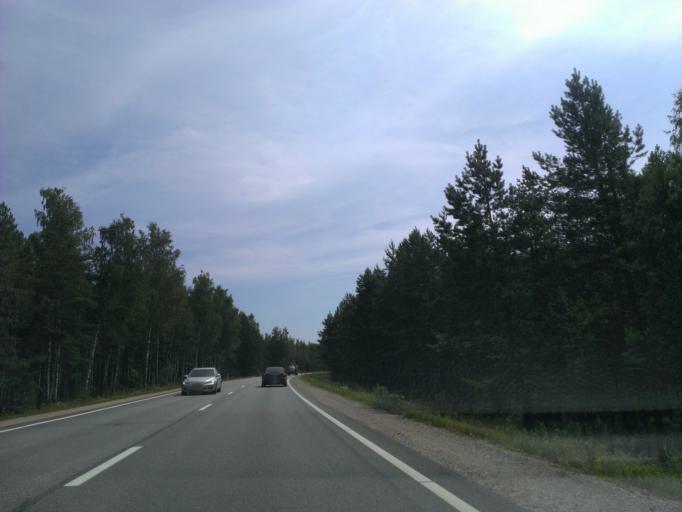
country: LV
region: Riga
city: Bergi
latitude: 56.9638
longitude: 24.3698
